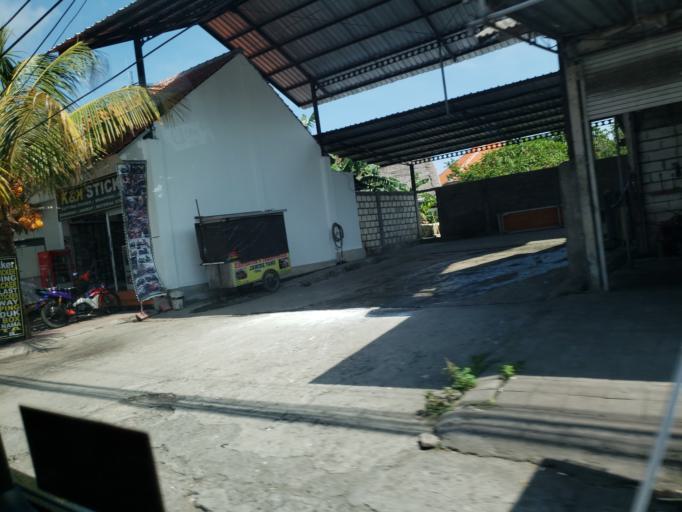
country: ID
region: Bali
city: Kangin
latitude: -8.8290
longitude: 115.1376
